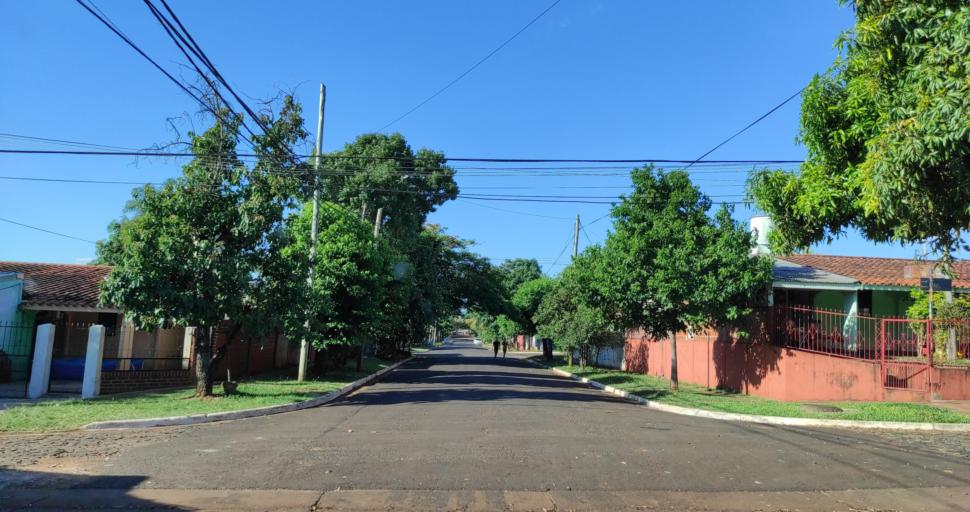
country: AR
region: Misiones
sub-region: Departamento de Capital
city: Posadas
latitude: -27.3764
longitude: -55.9311
